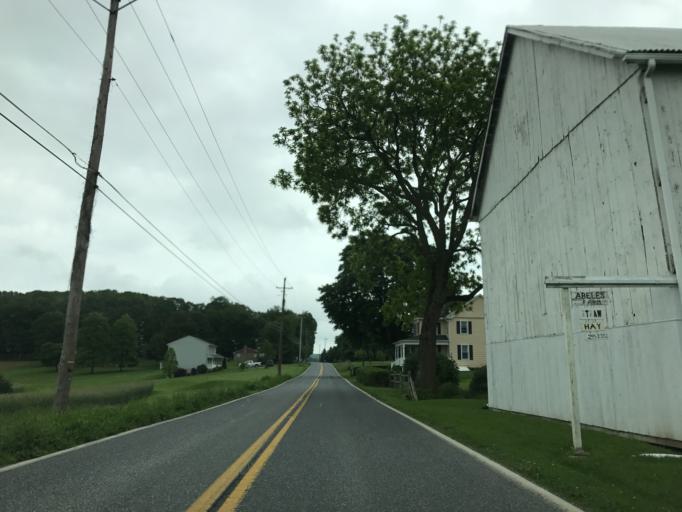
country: US
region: Pennsylvania
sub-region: York County
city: Dallastown
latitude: 39.8415
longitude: -76.6310
